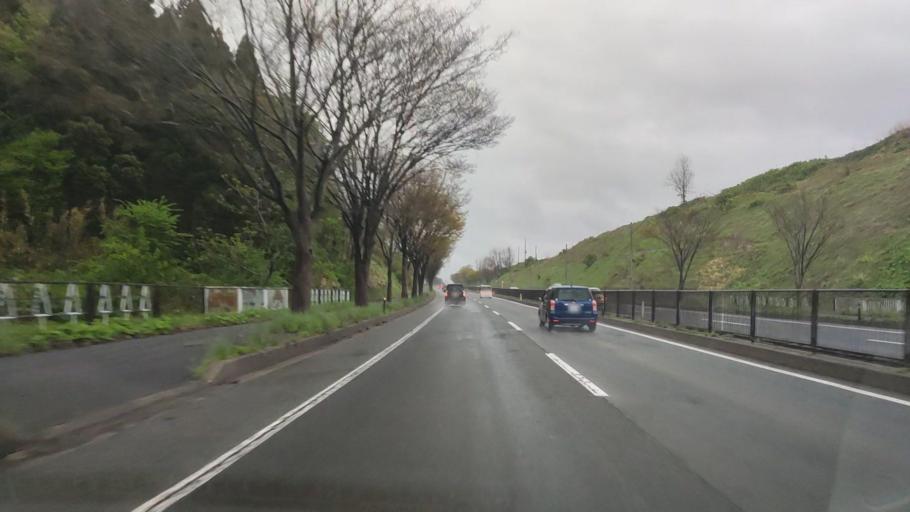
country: JP
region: Akita
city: Akita
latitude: 39.6729
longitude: 140.1555
